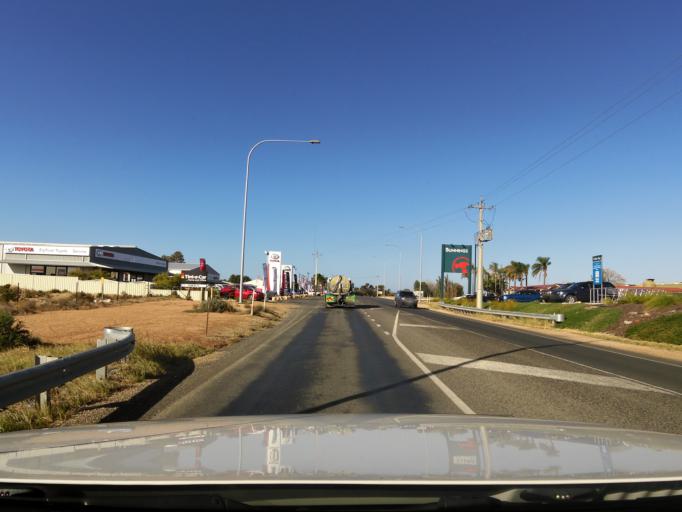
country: AU
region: South Australia
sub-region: Berri and Barmera
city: Berri
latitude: -34.2601
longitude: 140.6144
